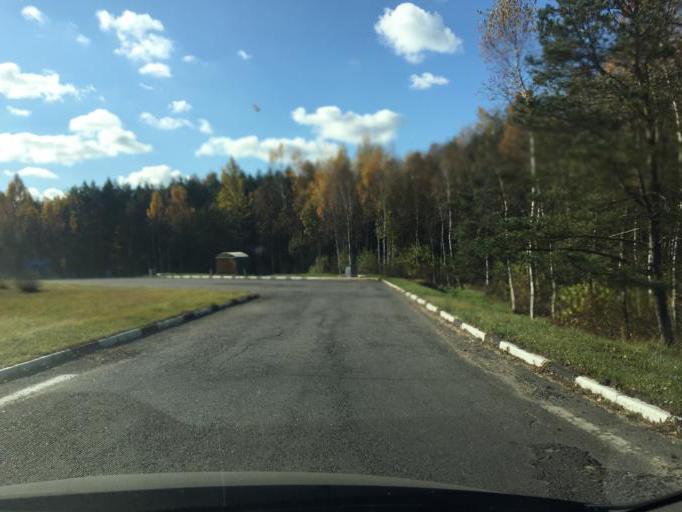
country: BY
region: Minsk
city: Slabada
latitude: 53.9338
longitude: 27.9612
